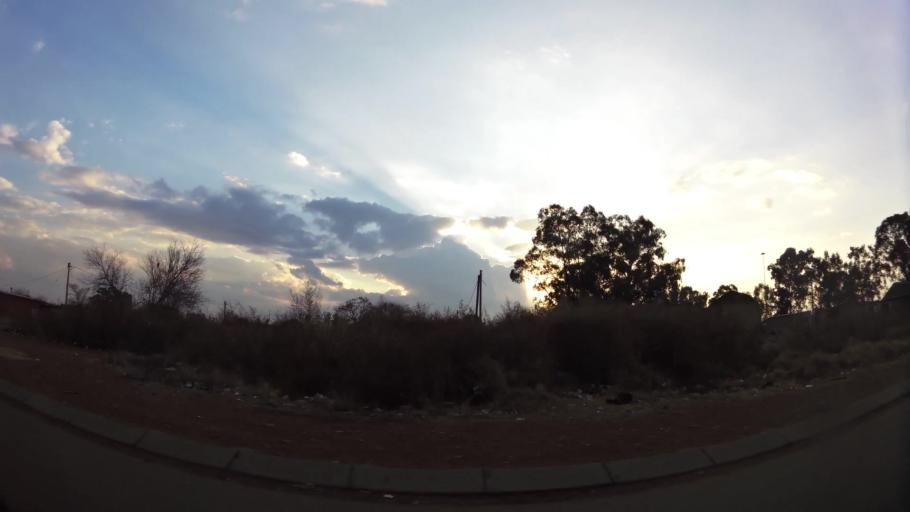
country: ZA
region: Gauteng
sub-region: City of Johannesburg Metropolitan Municipality
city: Orange Farm
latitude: -26.5380
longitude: 27.8500
